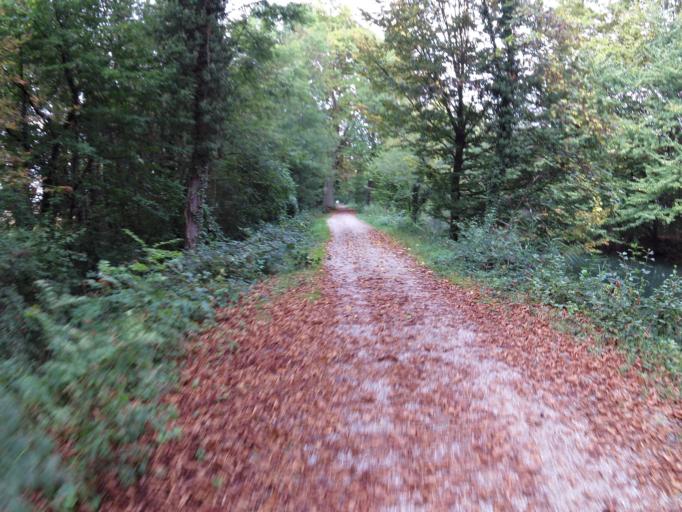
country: FR
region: Alsace
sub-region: Departement du Bas-Rhin
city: Marckolsheim
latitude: 48.1529
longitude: 7.5347
